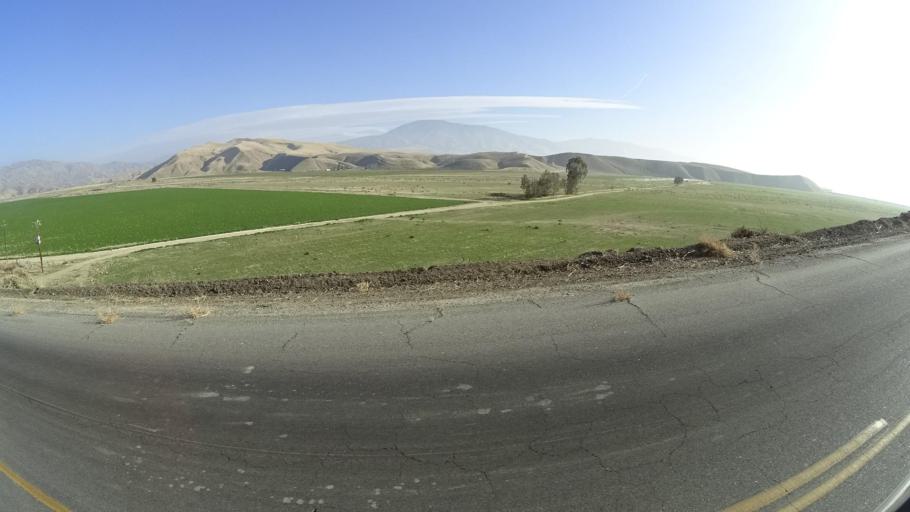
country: US
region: California
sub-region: Kern County
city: Arvin
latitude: 35.3259
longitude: -118.7744
